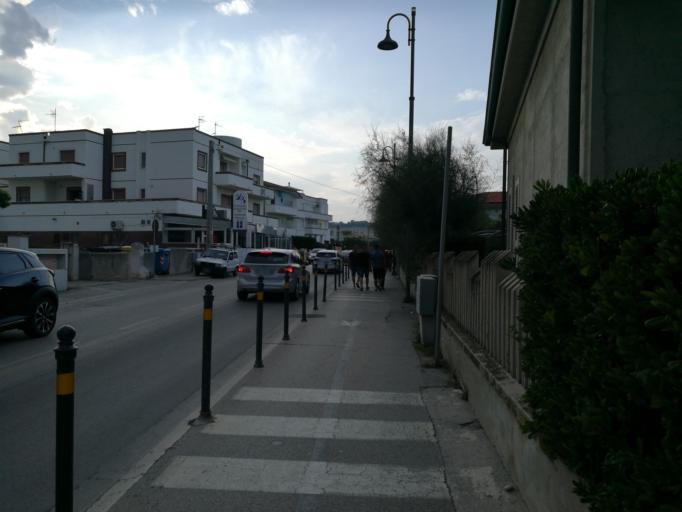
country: IT
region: Abruzzo
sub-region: Provincia di Chieti
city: Fossacesia
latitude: 42.2453
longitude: 14.5194
